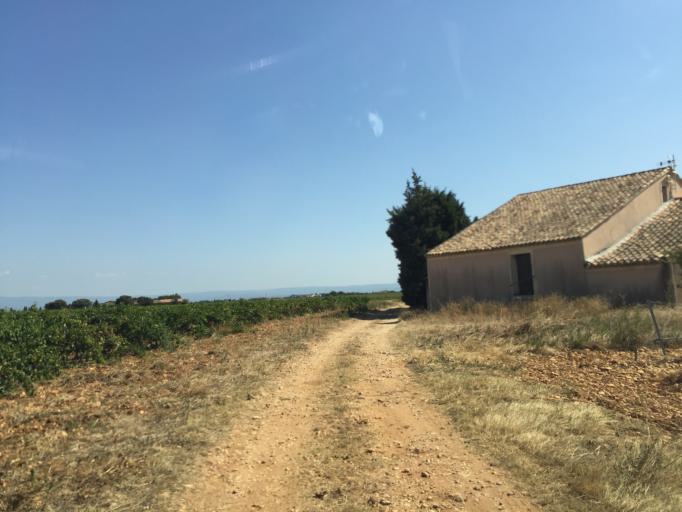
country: FR
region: Provence-Alpes-Cote d'Azur
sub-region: Departement du Vaucluse
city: Courthezon
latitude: 44.1053
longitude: 4.8428
